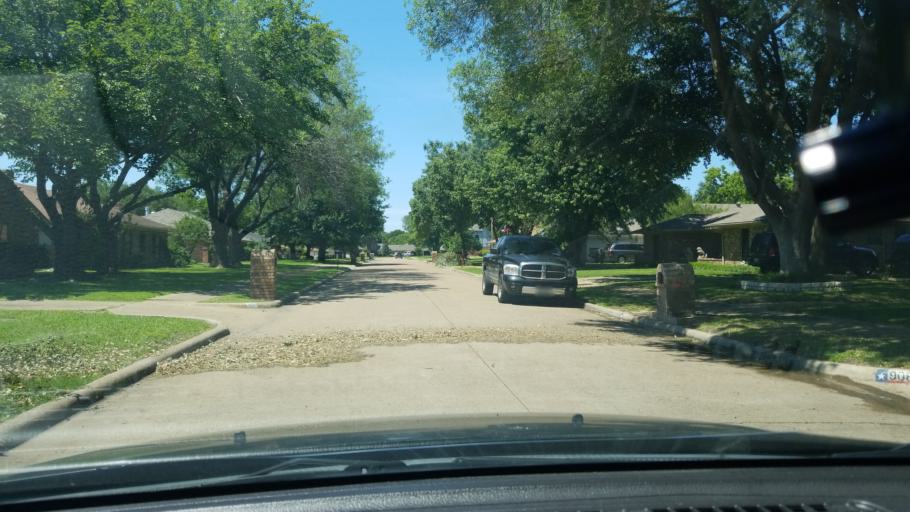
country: US
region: Texas
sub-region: Dallas County
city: Mesquite
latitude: 32.7570
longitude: -96.6031
